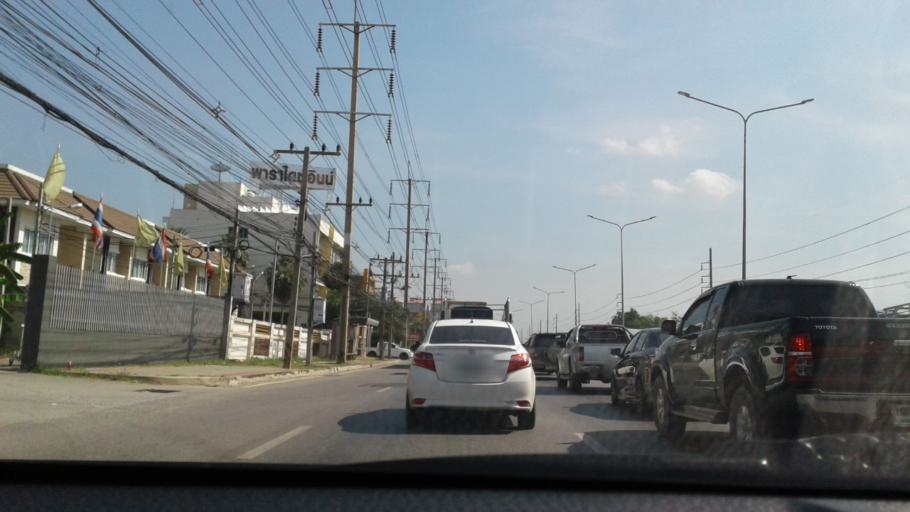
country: TH
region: Phra Nakhon Si Ayutthaya
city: Ban Bang Kadi Pathum Thani
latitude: 13.9764
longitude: 100.5831
